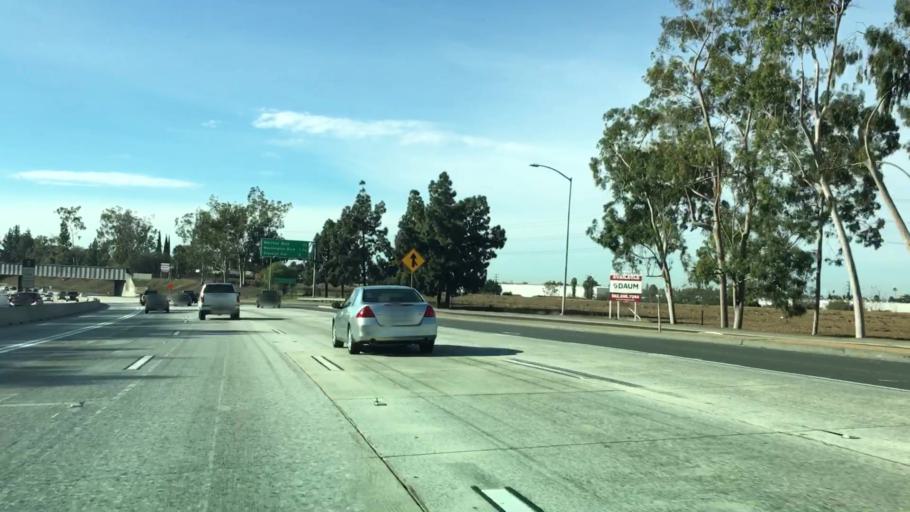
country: US
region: California
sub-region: Los Angeles County
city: West Whittier-Los Nietos
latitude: 34.0031
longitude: -118.0658
